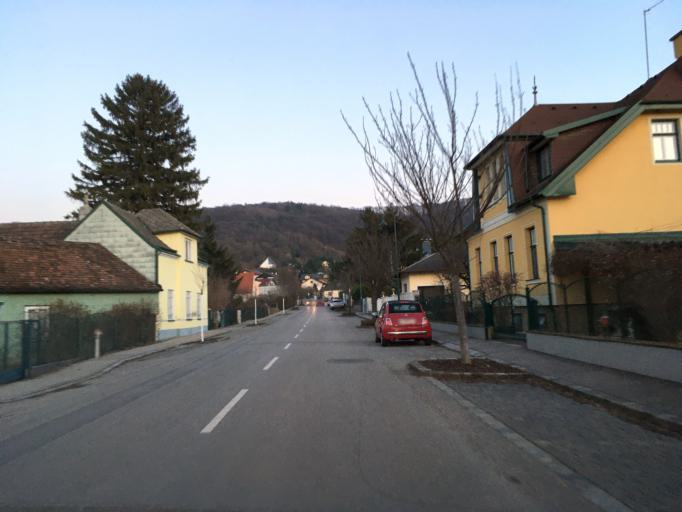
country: AT
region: Lower Austria
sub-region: Politischer Bezirk Tulln
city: Wordern
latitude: 48.3303
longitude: 16.2178
